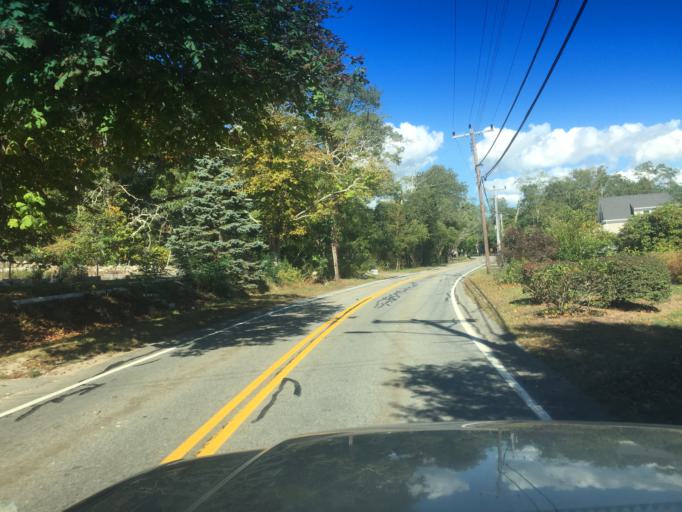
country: US
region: Massachusetts
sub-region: Barnstable County
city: North Falmouth
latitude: 41.6653
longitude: -70.6076
